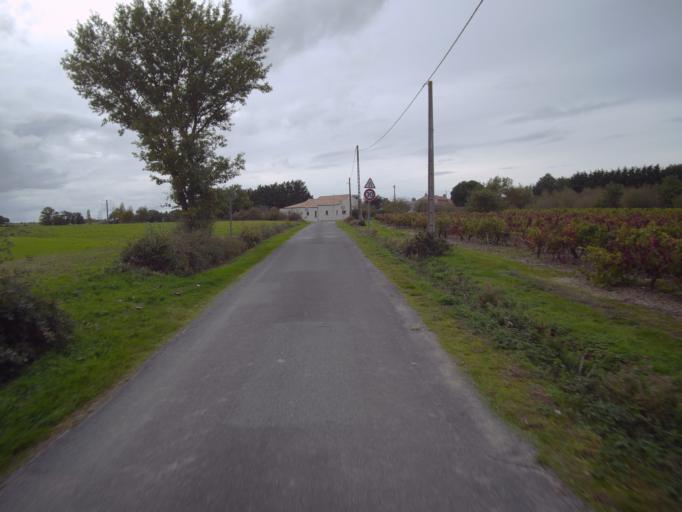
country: FR
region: Pays de la Loire
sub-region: Departement de la Loire-Atlantique
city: Remouille
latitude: 47.0303
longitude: -1.3863
